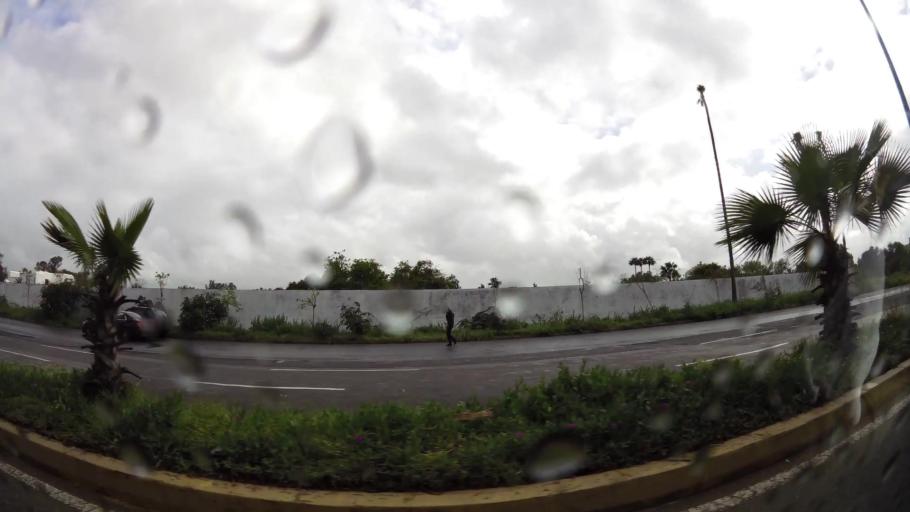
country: MA
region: Grand Casablanca
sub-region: Casablanca
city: Casablanca
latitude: 33.5310
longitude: -7.6282
